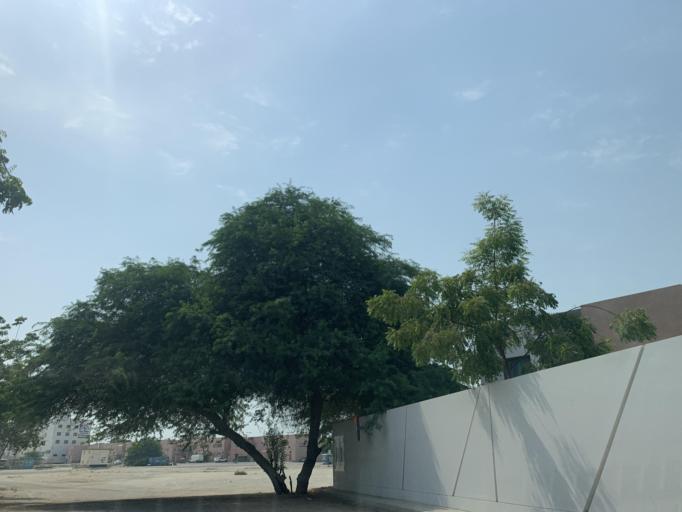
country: BH
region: Manama
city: Jidd Hafs
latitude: 26.2167
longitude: 50.4856
